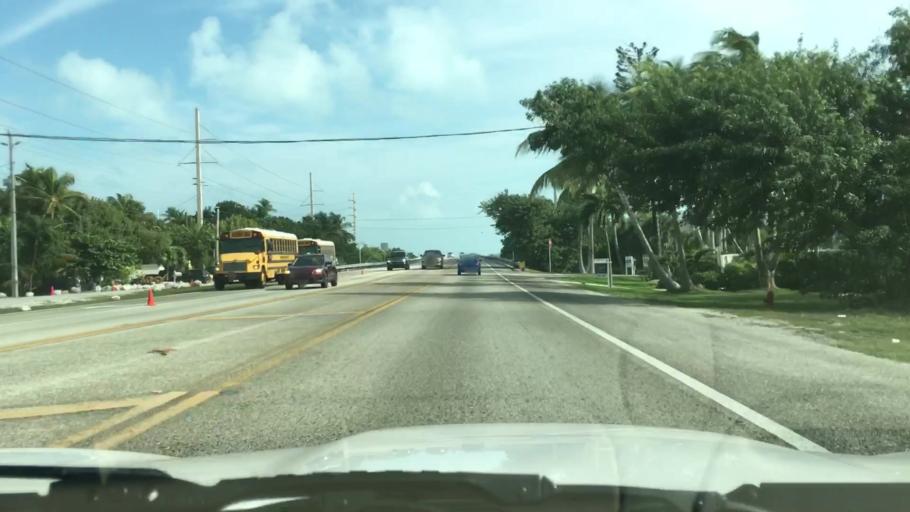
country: US
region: Florida
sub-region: Monroe County
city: Islamorada
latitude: 24.8814
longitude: -80.6923
